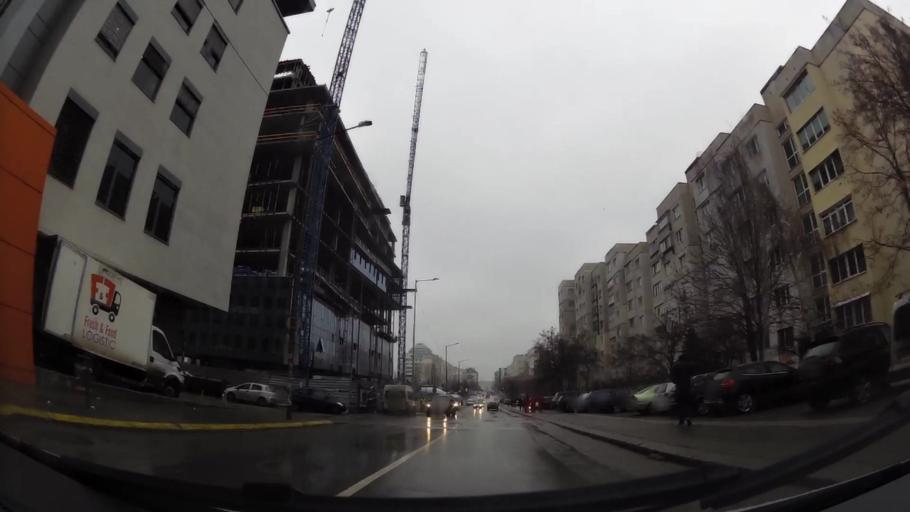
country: BG
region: Sofia-Capital
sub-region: Stolichna Obshtina
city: Sofia
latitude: 42.6287
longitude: 23.3750
